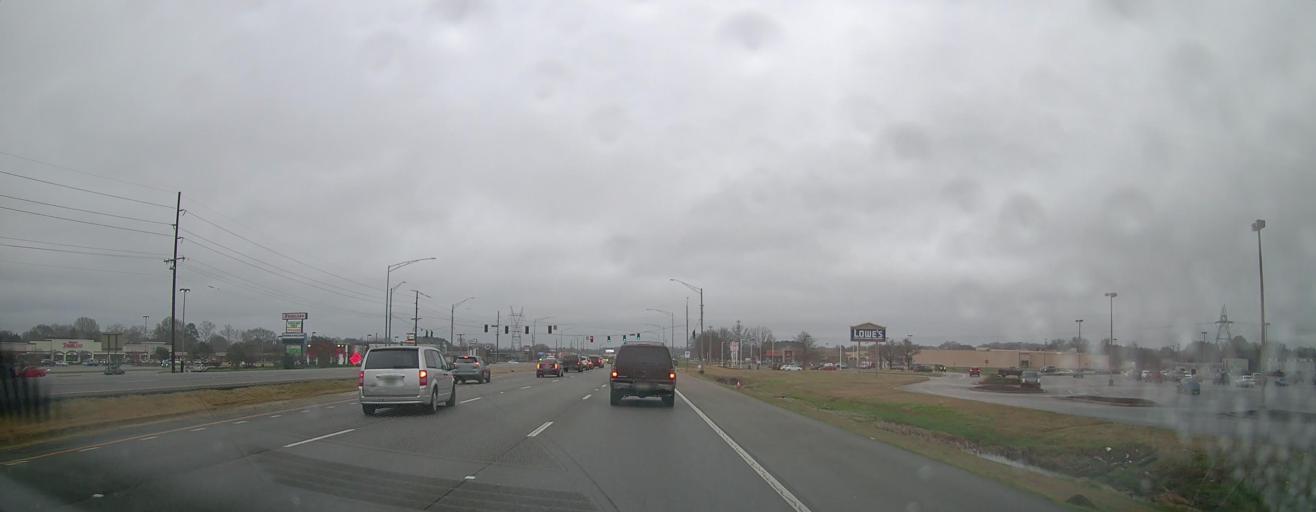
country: US
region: Alabama
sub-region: Morgan County
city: Decatur
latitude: 34.5690
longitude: -87.0129
